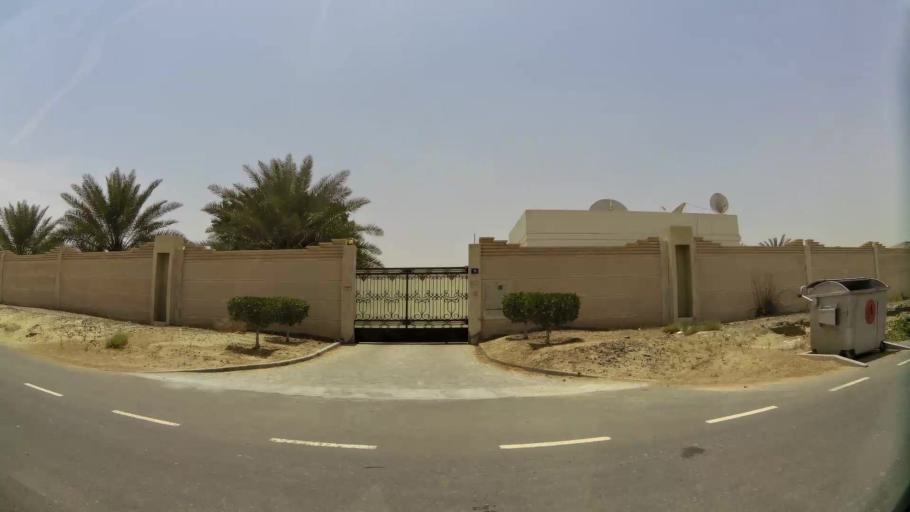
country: AE
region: Ash Shariqah
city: Sharjah
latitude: 25.2471
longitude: 55.4710
